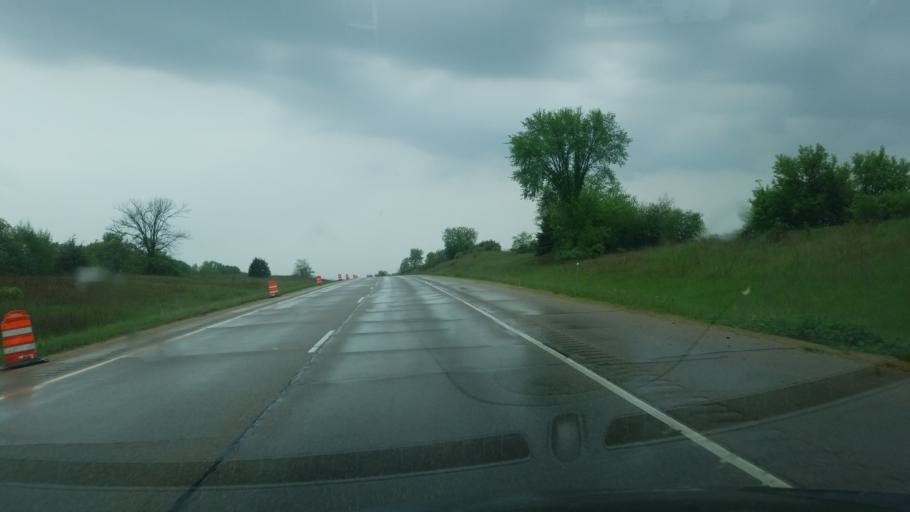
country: US
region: Wisconsin
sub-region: Dane County
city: Oregon
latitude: 42.9744
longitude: -89.3857
